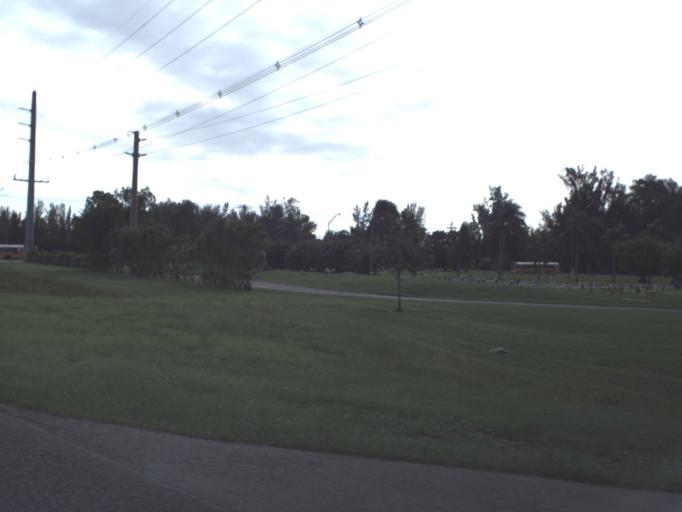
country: US
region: Florida
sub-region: Lee County
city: Cape Coral
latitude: 26.6381
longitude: -82.0090
